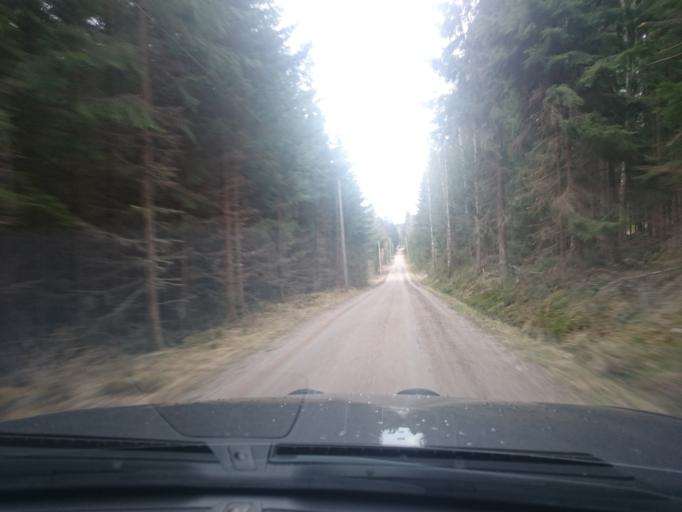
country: SE
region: Joenkoeping
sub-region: Vetlanda Kommun
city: Vetlanda
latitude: 57.2954
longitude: 15.1398
